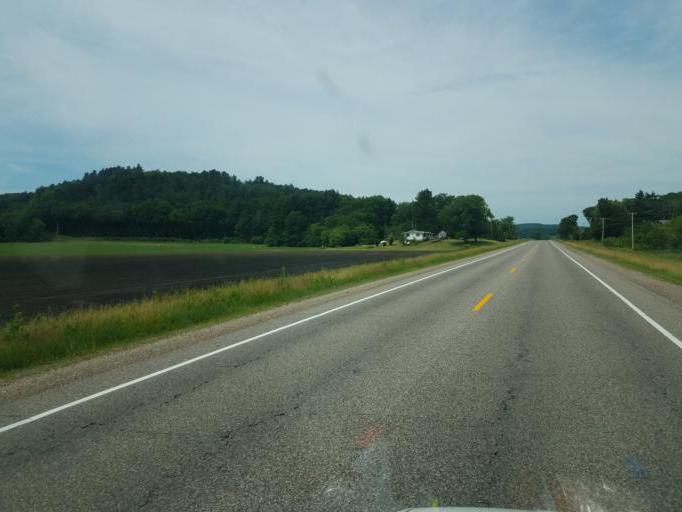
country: US
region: Wisconsin
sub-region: Juneau County
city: Mauston
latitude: 43.7892
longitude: -90.1480
